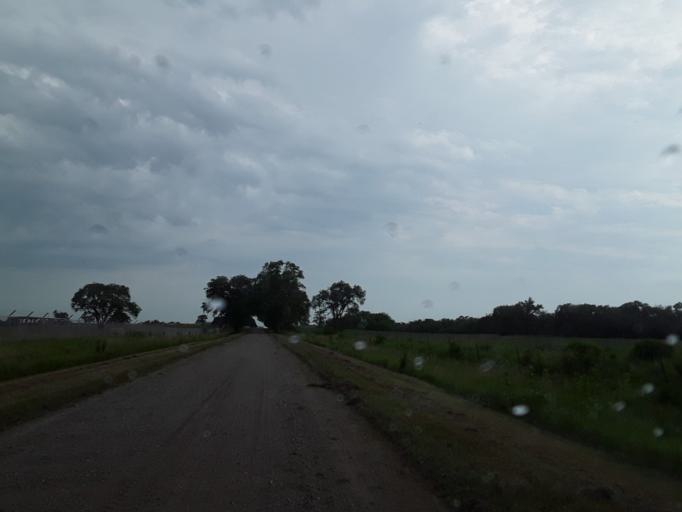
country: US
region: Nebraska
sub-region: Saunders County
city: Yutan
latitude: 41.1940
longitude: -96.4450
